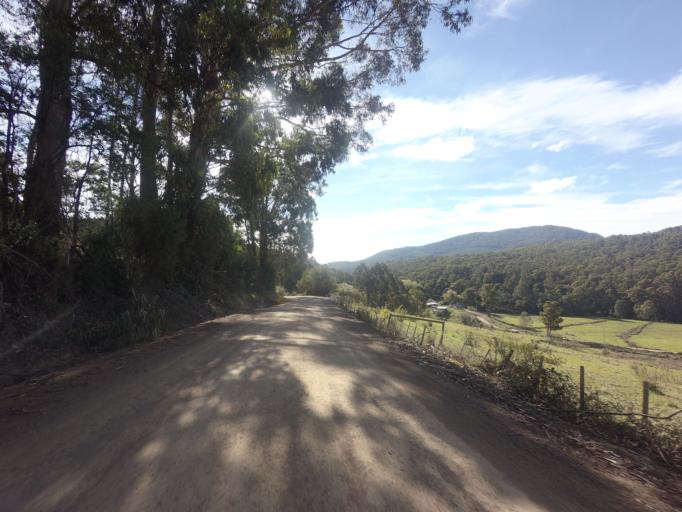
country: AU
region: Tasmania
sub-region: Clarence
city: Sandford
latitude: -43.1373
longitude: 147.7672
